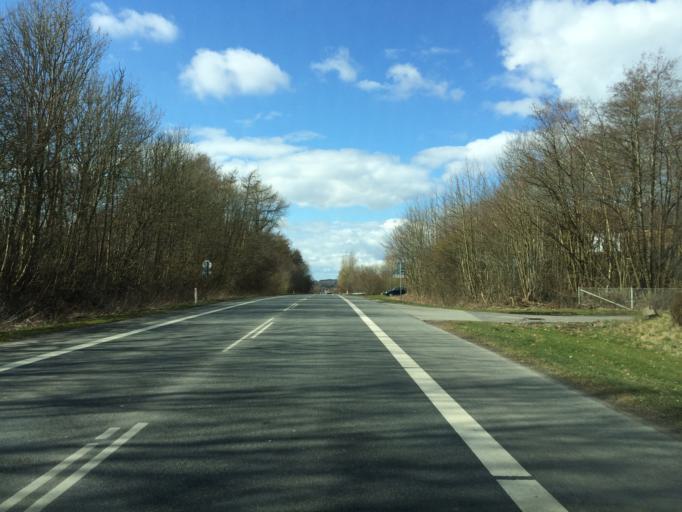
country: DK
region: South Denmark
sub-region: Assens Kommune
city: Vissenbjerg
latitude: 55.3937
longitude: 10.1086
